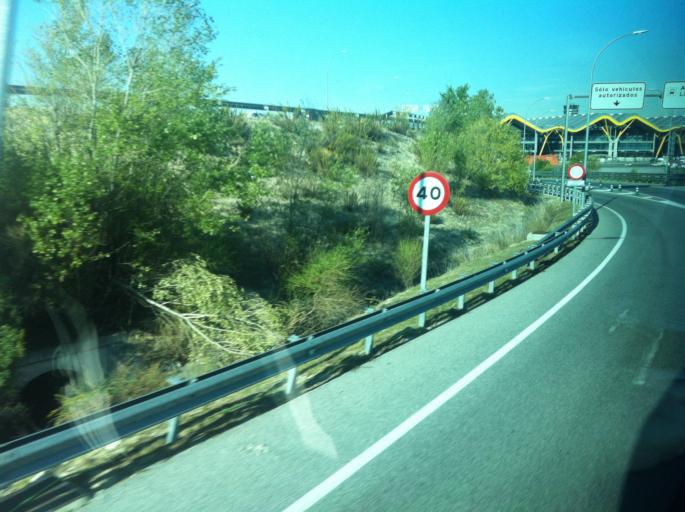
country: ES
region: Madrid
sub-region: Provincia de Madrid
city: Barajas de Madrid
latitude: 40.4866
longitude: -3.5941
